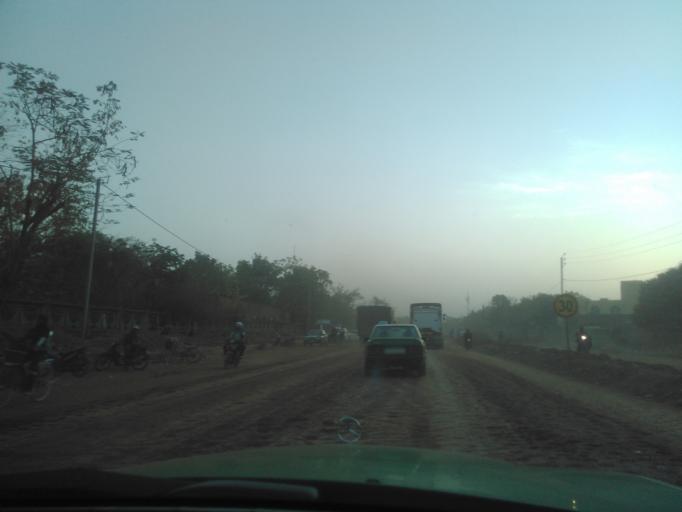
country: BF
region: Centre
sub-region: Kadiogo Province
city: Ouagadougou
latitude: 12.3822
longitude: -1.5061
